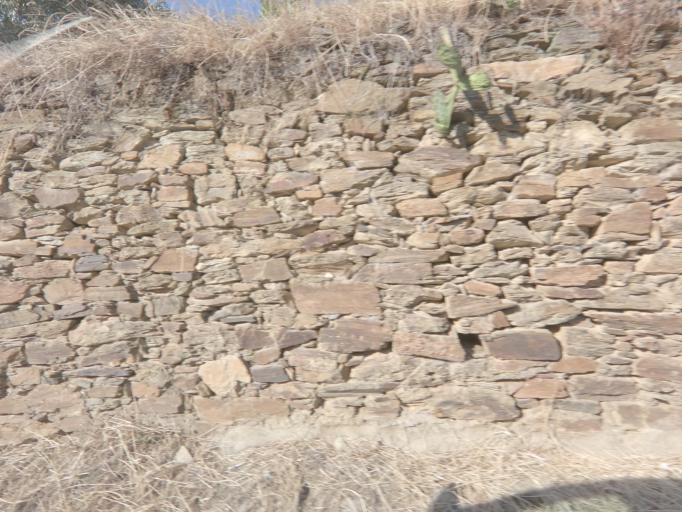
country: PT
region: Vila Real
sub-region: Sabrosa
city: Vilela
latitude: 41.1795
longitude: -7.5798
